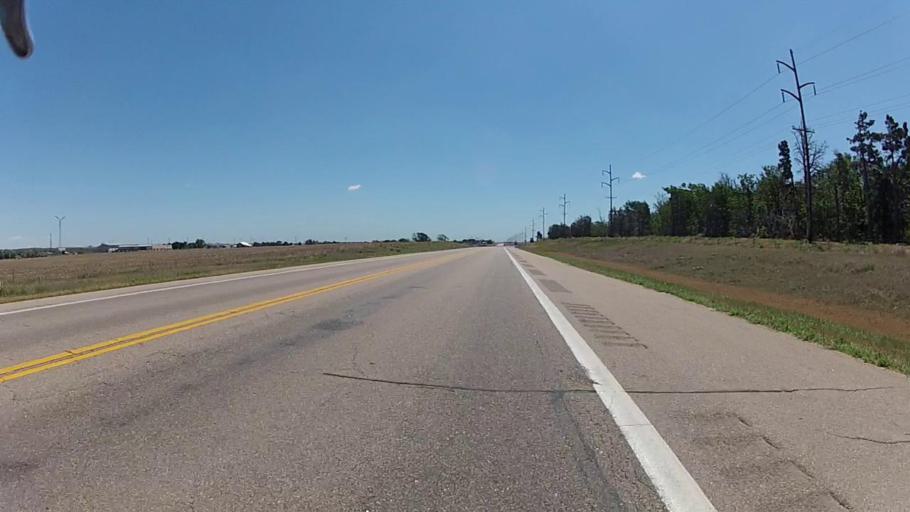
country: US
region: Kansas
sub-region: Ford County
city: Dodge City
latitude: 37.7222
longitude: -100.0380
